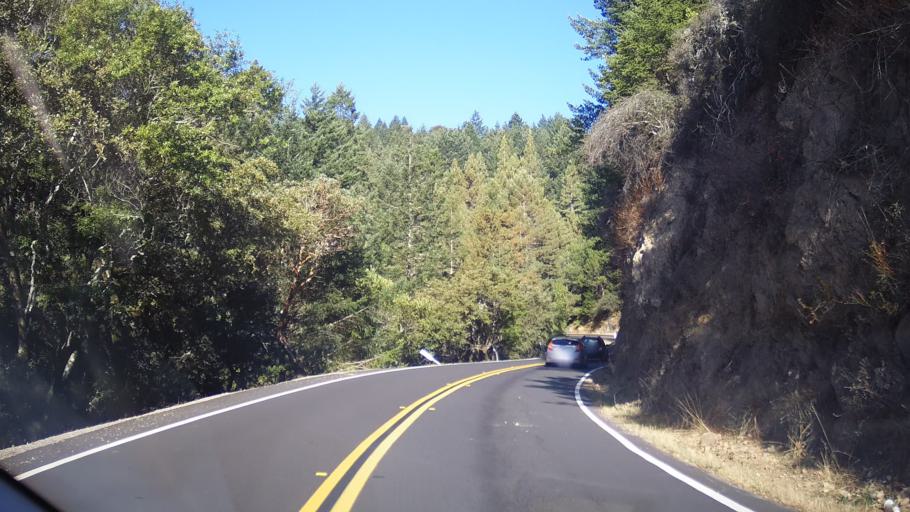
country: US
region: California
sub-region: Marin County
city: Mill Valley
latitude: 37.9121
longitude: -122.5960
